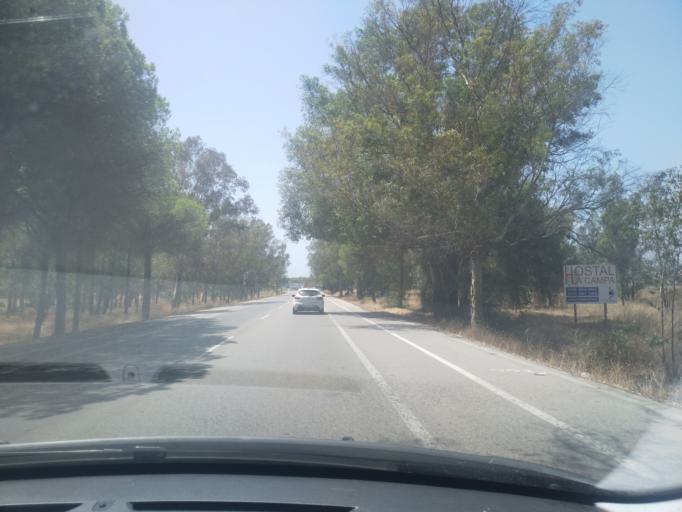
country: ES
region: Andalusia
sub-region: Provincia de Cadiz
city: Chiclana de la Frontera
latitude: 36.3906
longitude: -6.1293
